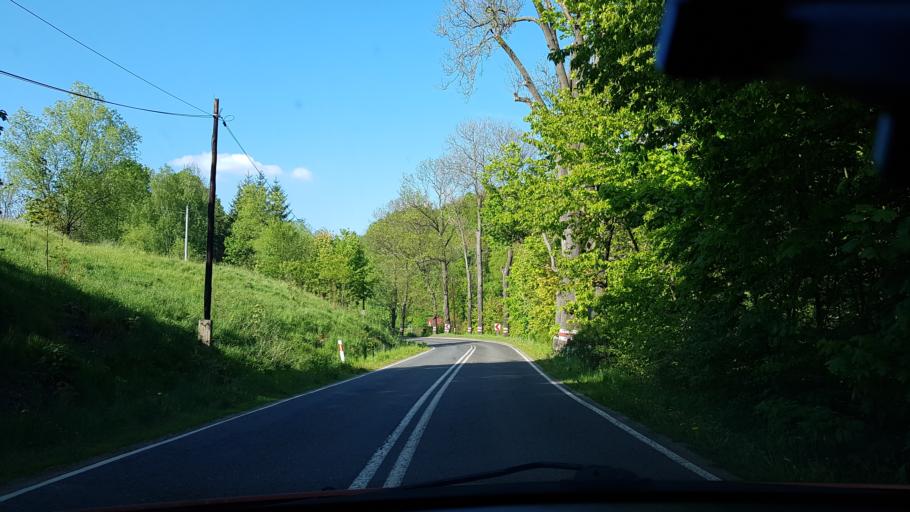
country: PL
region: Lower Silesian Voivodeship
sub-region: Powiat klodzki
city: Nowa Ruda
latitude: 50.5653
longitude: 16.4723
